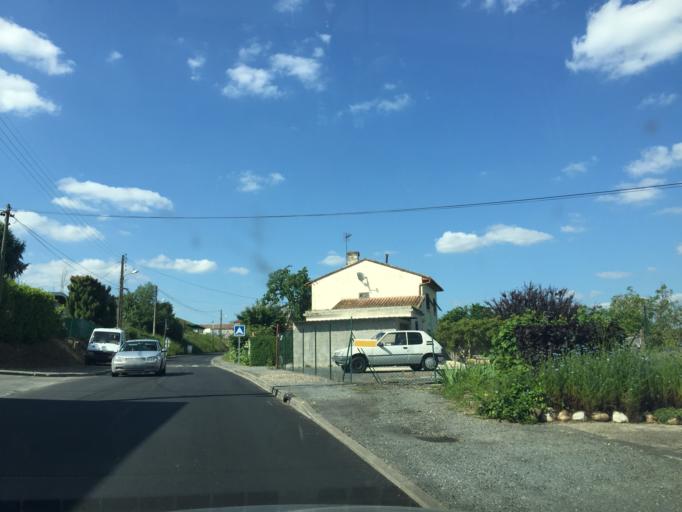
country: FR
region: Aquitaine
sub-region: Departement de la Gironde
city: La Reole
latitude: 44.5897
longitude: -0.0336
